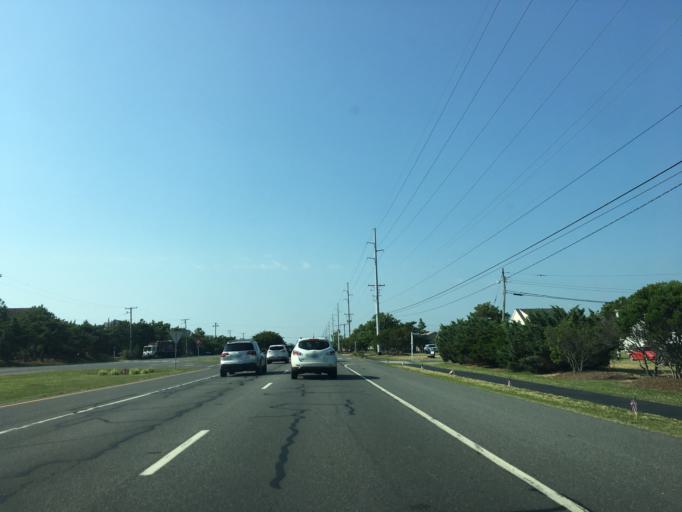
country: US
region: Delaware
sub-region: Sussex County
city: Bethany Beach
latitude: 38.5191
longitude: -75.0552
